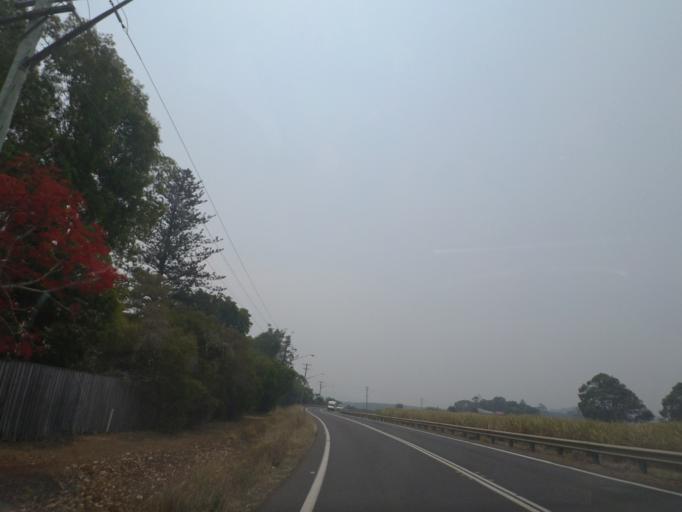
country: AU
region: New South Wales
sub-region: Richmond Valley
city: Evans Head
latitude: -29.0070
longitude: 153.4367
